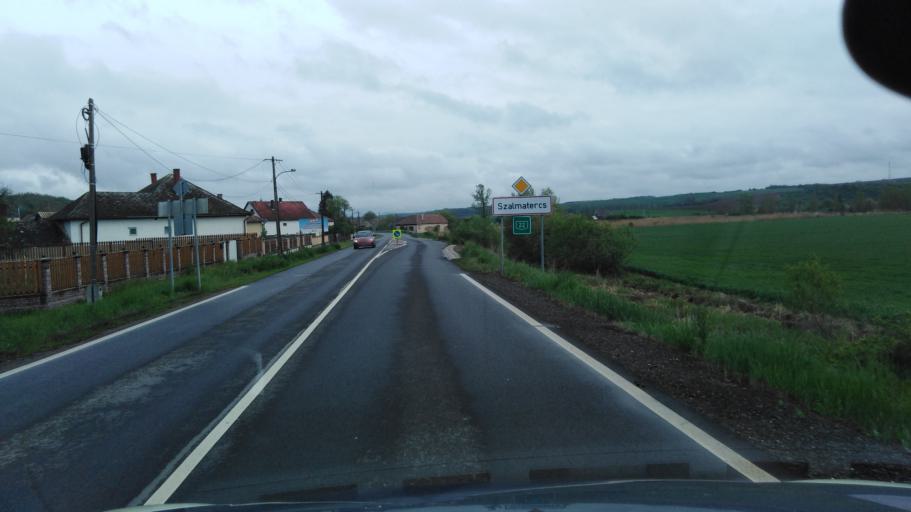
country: HU
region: Nograd
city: Karancskeszi
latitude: 48.1261
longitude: 19.6316
